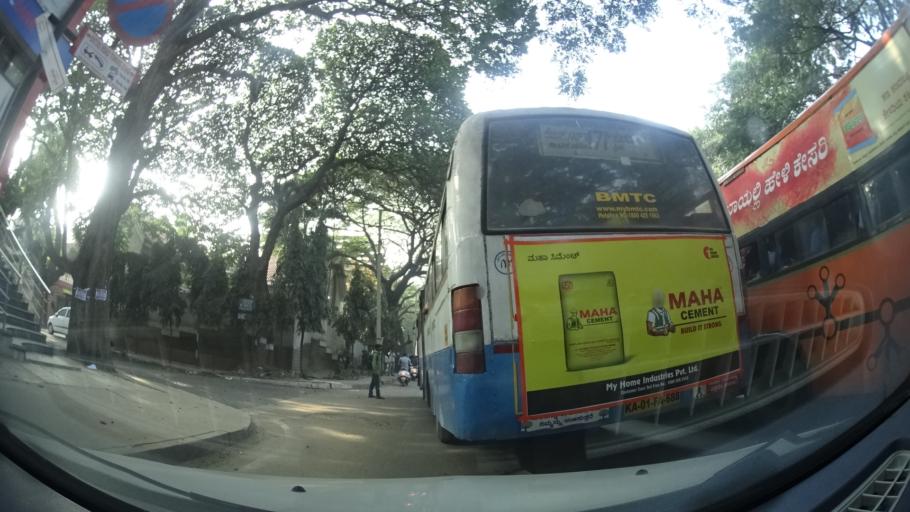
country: IN
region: Karnataka
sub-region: Bangalore Urban
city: Bangalore
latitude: 12.9294
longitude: 77.6213
